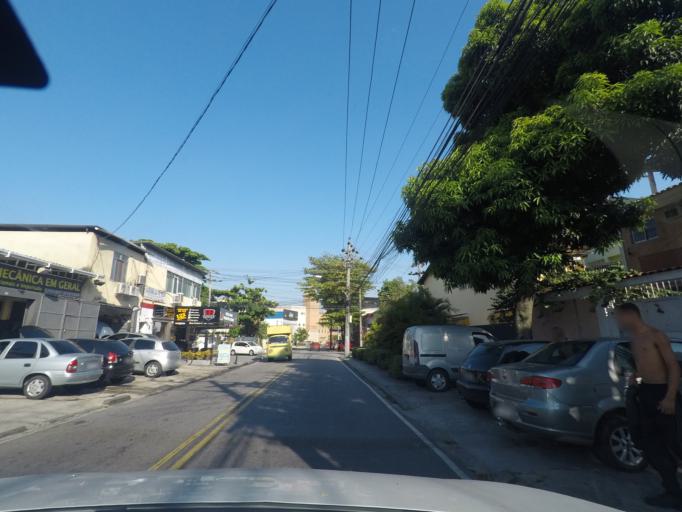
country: BR
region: Rio de Janeiro
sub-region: Duque De Caxias
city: Duque de Caxias
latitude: -22.8295
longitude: -43.2839
